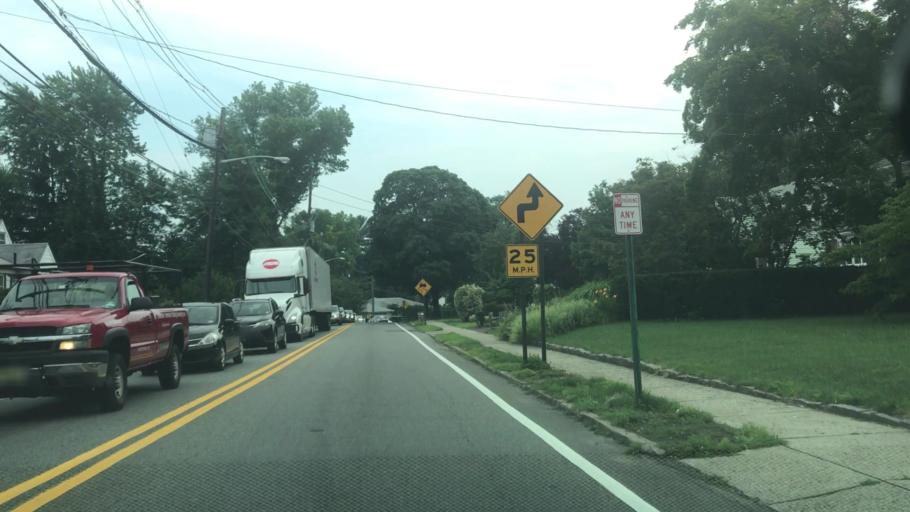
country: US
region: New Jersey
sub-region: Bergen County
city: Fair Lawn
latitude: 40.9265
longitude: -74.1297
